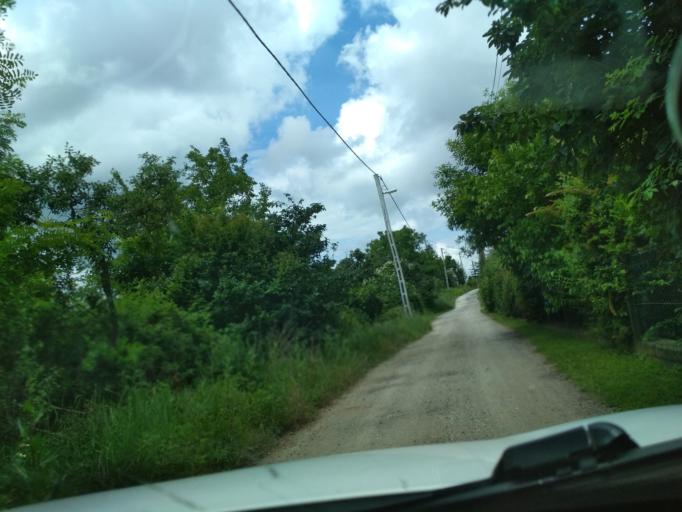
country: HU
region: Jasz-Nagykun-Szolnok
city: Tiszafured
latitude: 47.6068
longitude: 20.7467
